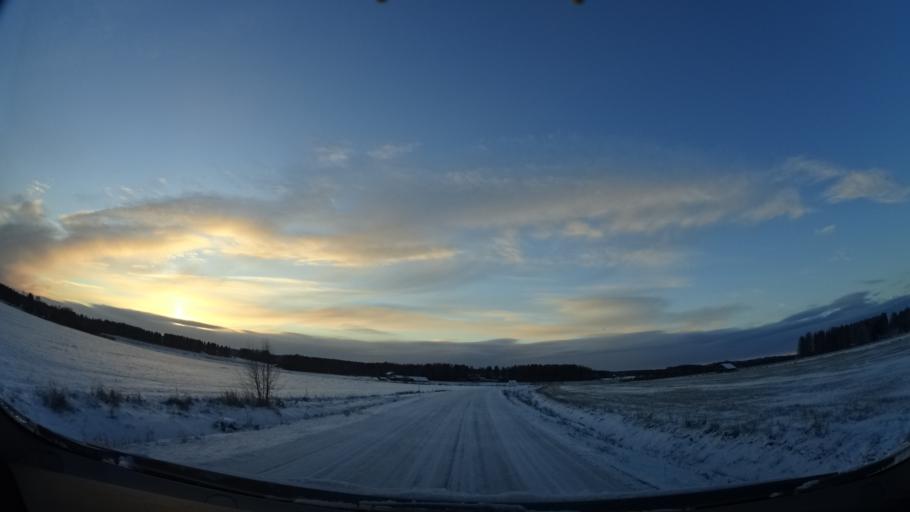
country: SE
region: Vaesterbotten
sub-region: Skelleftea Kommun
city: Kage
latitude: 64.8500
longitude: 20.9879
